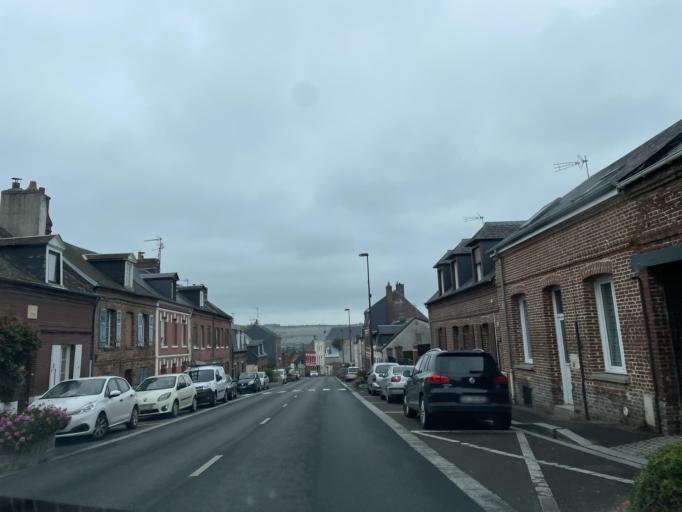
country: FR
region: Haute-Normandie
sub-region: Departement de la Seine-Maritime
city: Eu
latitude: 50.0415
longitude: 1.4175
